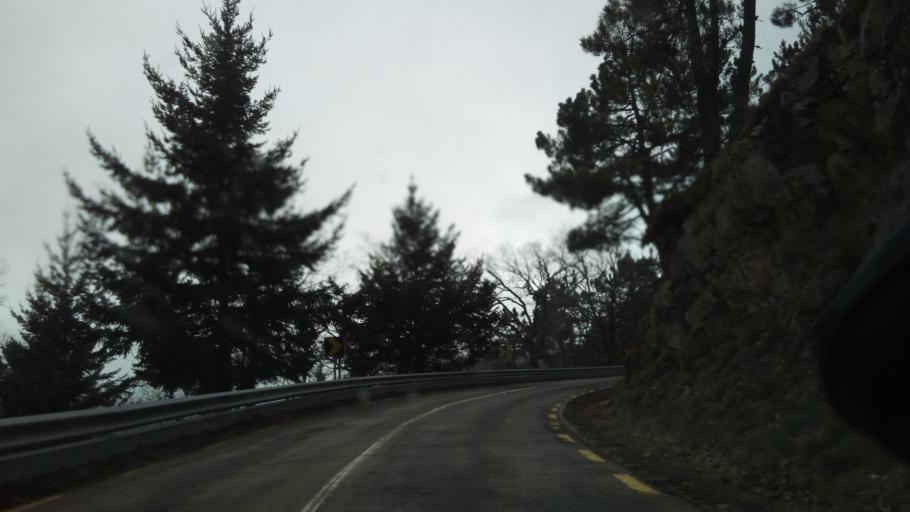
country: PT
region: Guarda
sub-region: Manteigas
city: Manteigas
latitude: 40.4170
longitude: -7.5459
